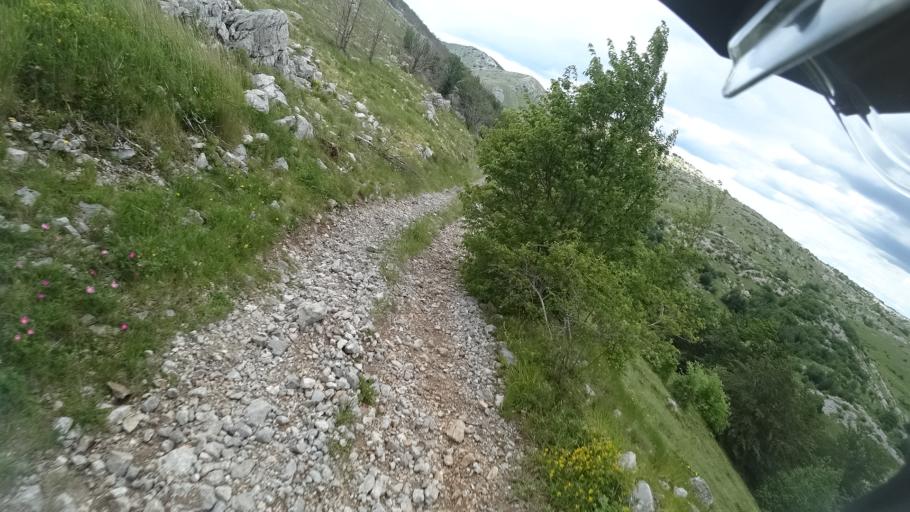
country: HR
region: Zadarska
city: Obrovac
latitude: 44.2613
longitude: 15.7257
